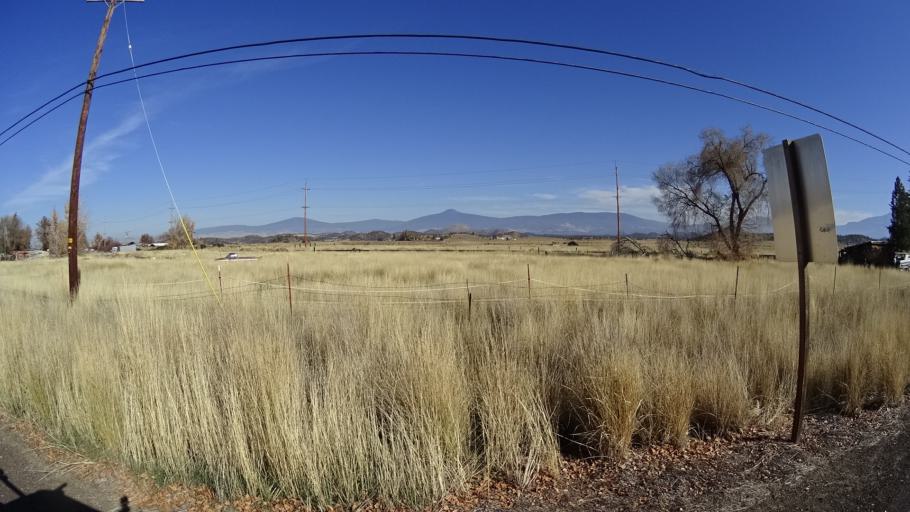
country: US
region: California
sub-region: Siskiyou County
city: Montague
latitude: 41.6395
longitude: -122.5221
